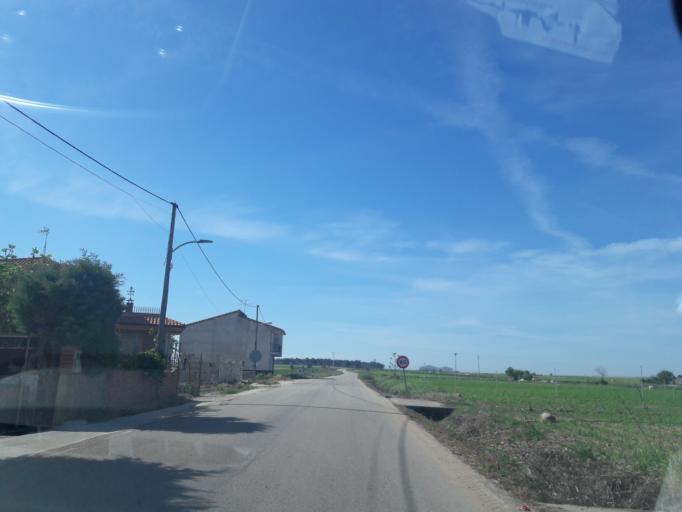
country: ES
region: Castille and Leon
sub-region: Provincia de Salamanca
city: Villoruela
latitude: 41.0449
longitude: -5.3870
